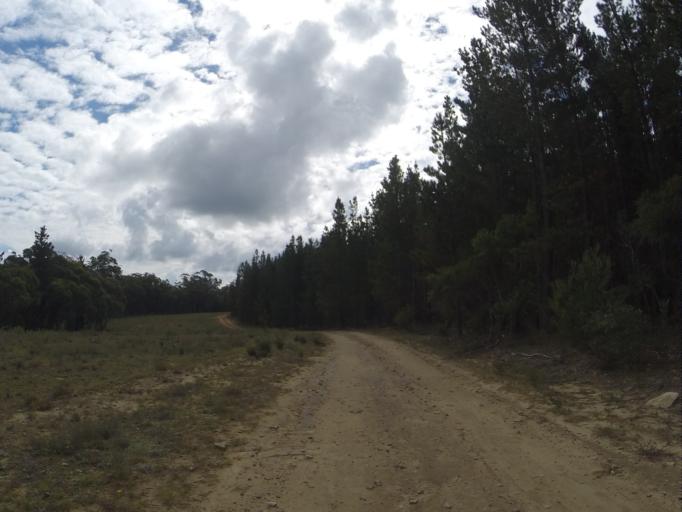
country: AU
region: New South Wales
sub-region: Wingecarribee
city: Moss Vale
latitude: -34.5163
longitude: 150.2275
